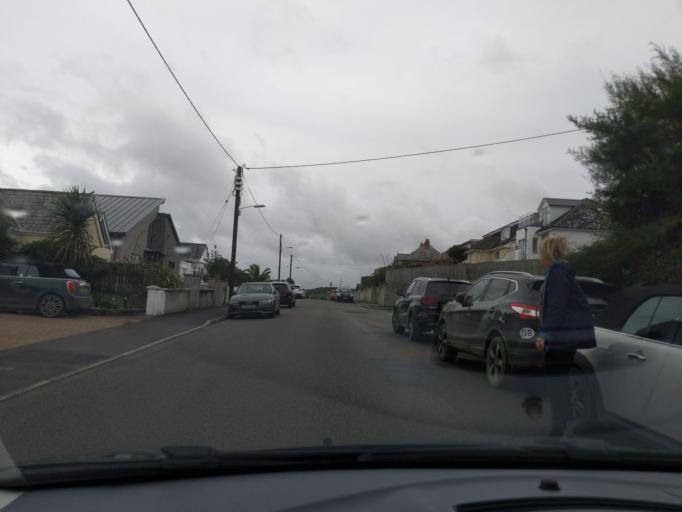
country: GB
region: England
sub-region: Cornwall
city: Padstow
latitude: 50.5372
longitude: -4.9373
